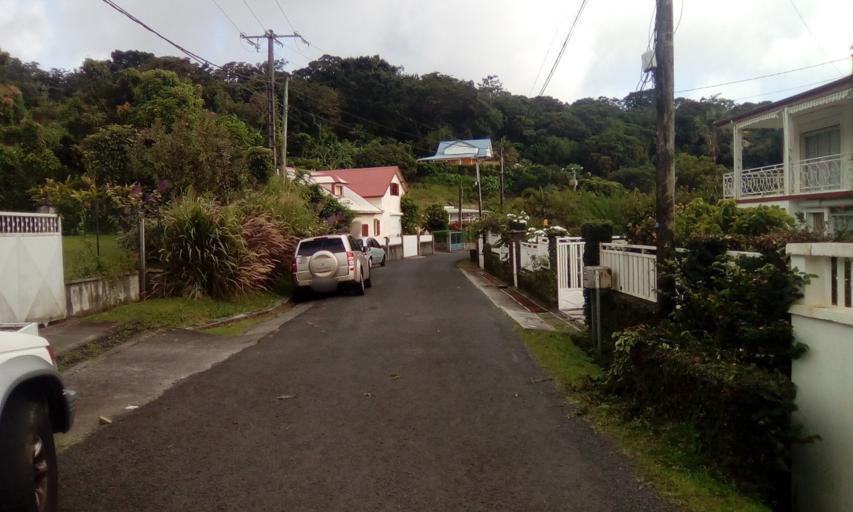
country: GP
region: Guadeloupe
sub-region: Guadeloupe
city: Saint-Claude
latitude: 16.0287
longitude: -61.6860
